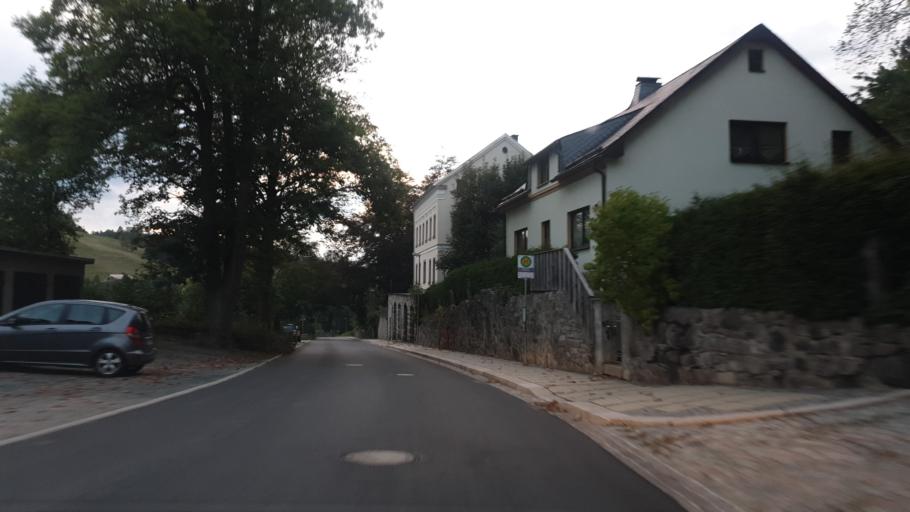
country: DE
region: Saxony
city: Eibenstock
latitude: 50.4949
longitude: 12.5947
